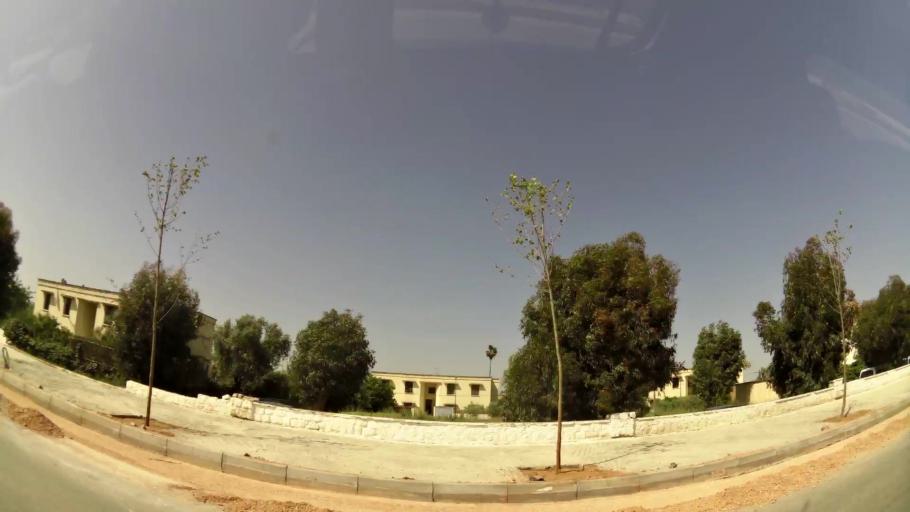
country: MA
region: Meknes-Tafilalet
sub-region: Meknes
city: Meknes
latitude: 33.8859
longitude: -5.5389
